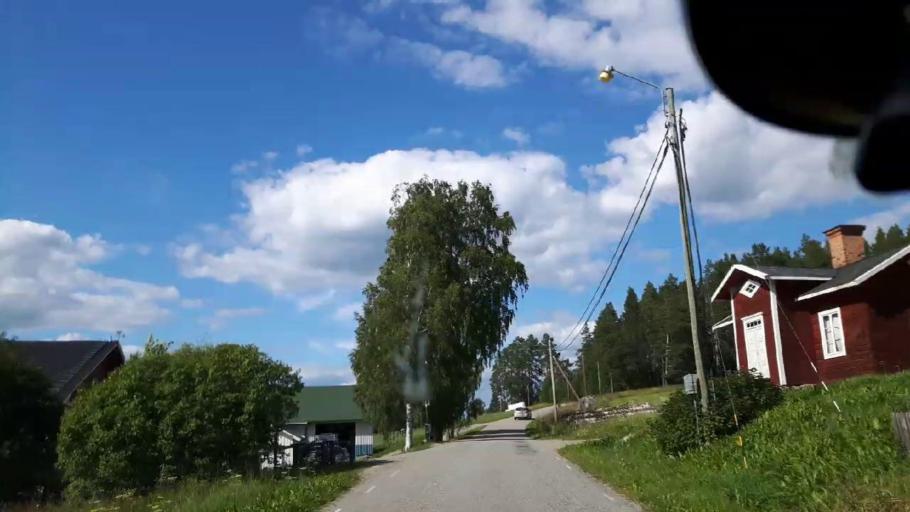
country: SE
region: Jaemtland
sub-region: Braecke Kommun
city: Braecke
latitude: 62.8701
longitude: 15.2721
